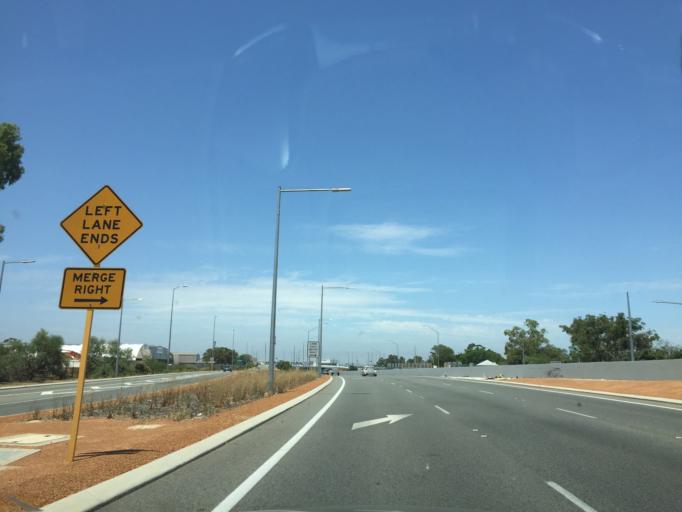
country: AU
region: Western Australia
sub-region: Belmont
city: Kewdale
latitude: -31.9694
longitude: 115.9525
